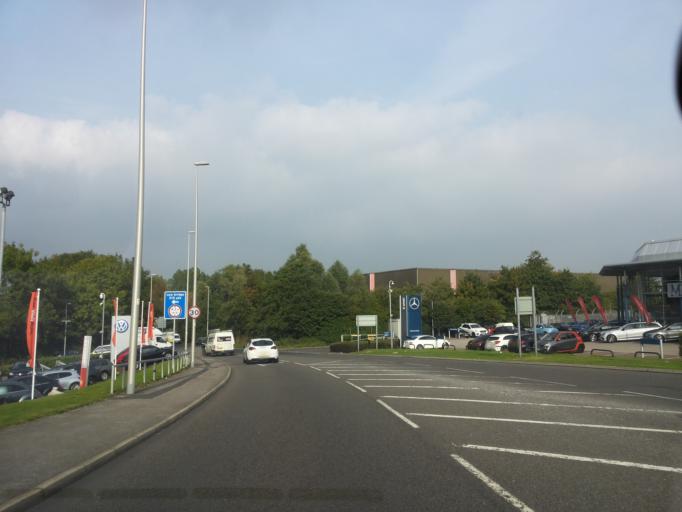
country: GB
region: England
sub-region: Lancashire
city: Great Marton
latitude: 53.7946
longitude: -3.0023
